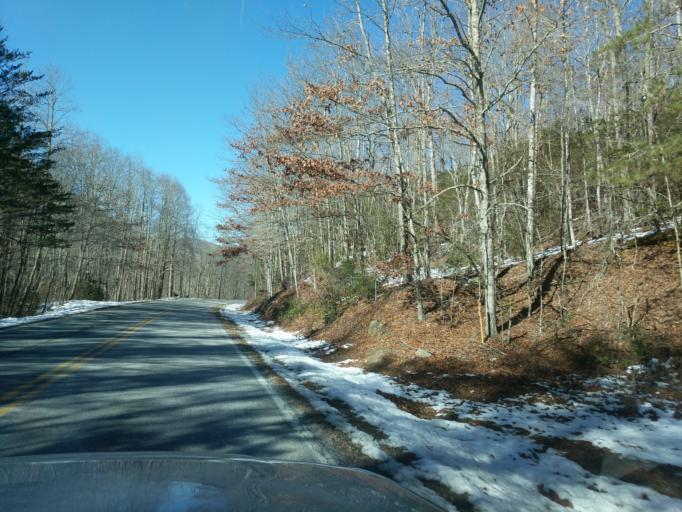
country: US
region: Georgia
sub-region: Towns County
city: Hiawassee
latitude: 34.9137
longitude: -83.6210
